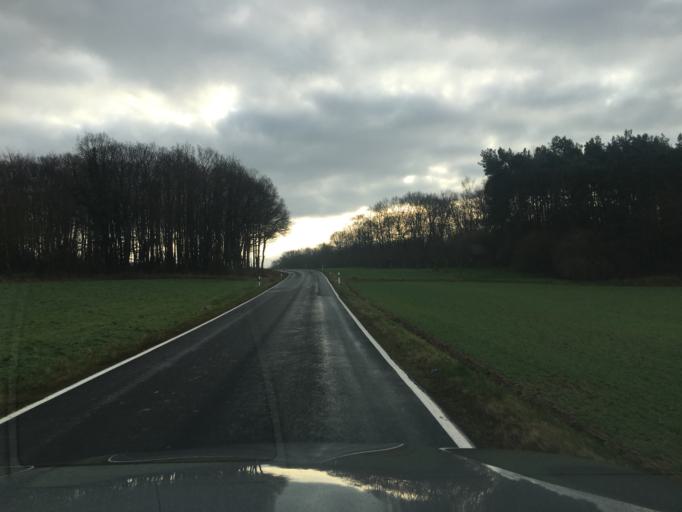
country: DE
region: Rheinland-Pfalz
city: Unkel
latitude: 50.5885
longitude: 7.1575
